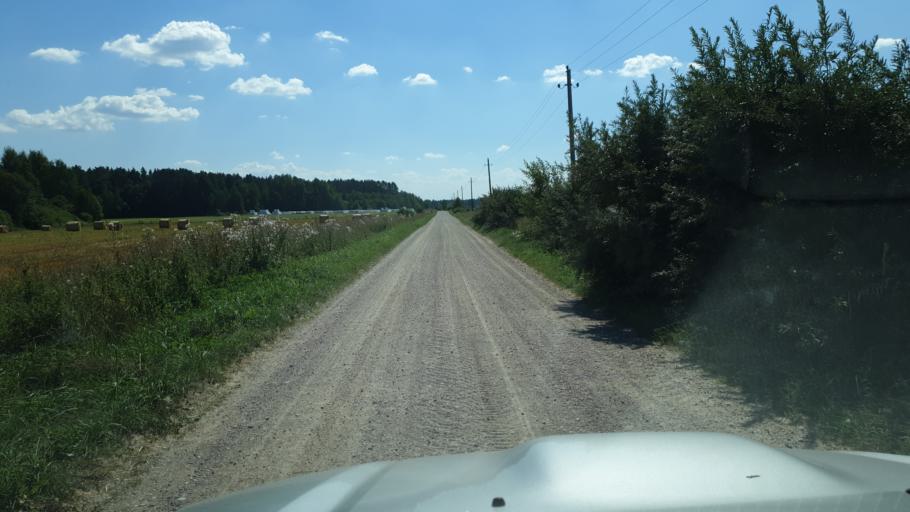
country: LT
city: Sirvintos
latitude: 54.9156
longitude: 24.9118
